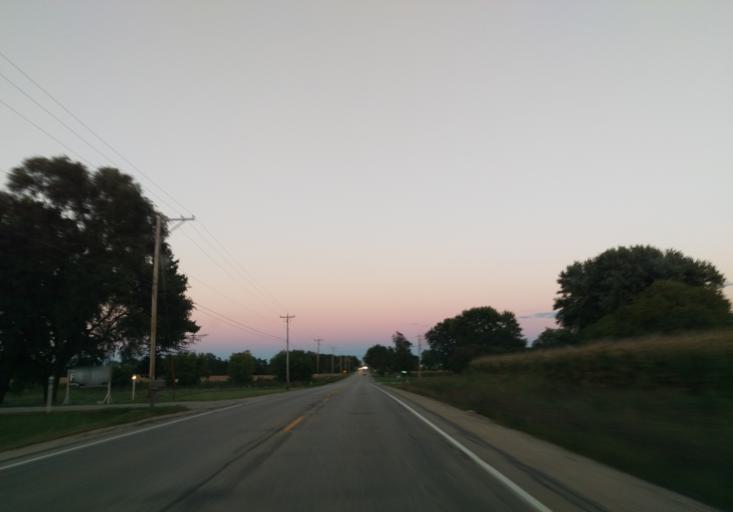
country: US
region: Wisconsin
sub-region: Rock County
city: Janesville
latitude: 42.7303
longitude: -89.0938
